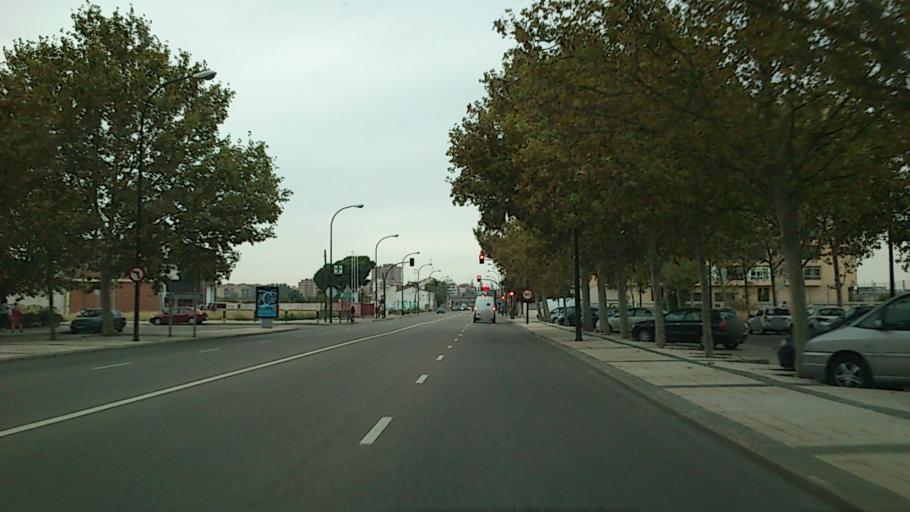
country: ES
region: Aragon
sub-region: Provincia de Zaragoza
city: Zaragoza
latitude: 41.6699
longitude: -0.8468
